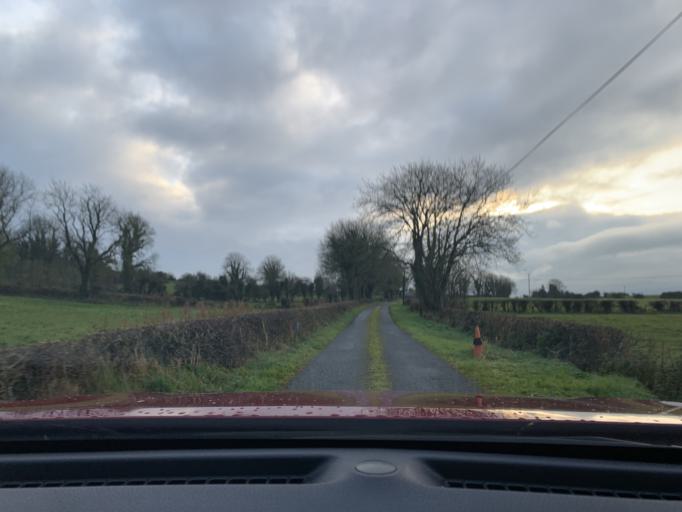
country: IE
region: Connaught
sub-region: Sligo
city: Ballymote
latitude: 54.0370
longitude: -8.5444
